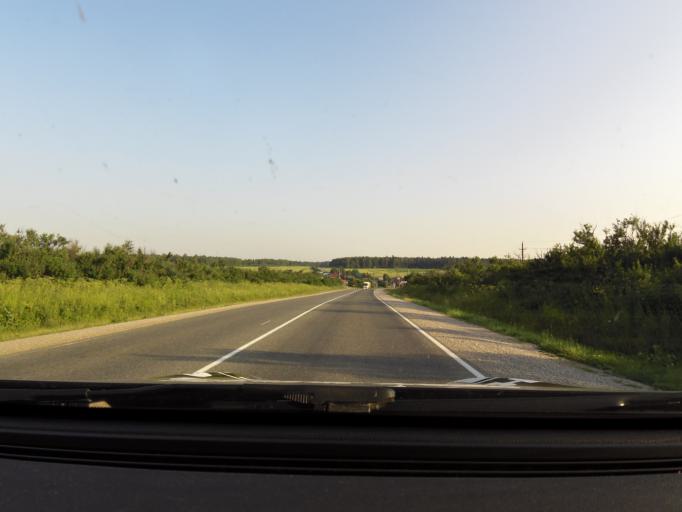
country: RU
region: Sverdlovsk
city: Nizhniye Sergi
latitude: 56.5594
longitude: 59.2160
